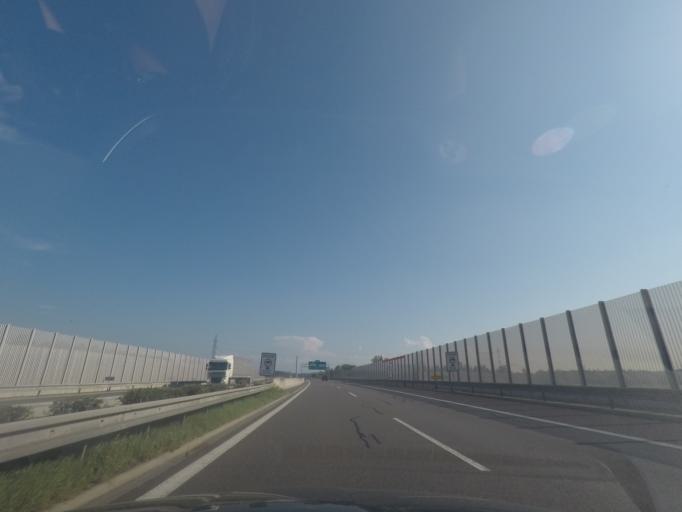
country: PL
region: Silesian Voivodeship
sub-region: Powiat raciborski
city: Chalupki
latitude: 49.8932
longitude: 18.3034
